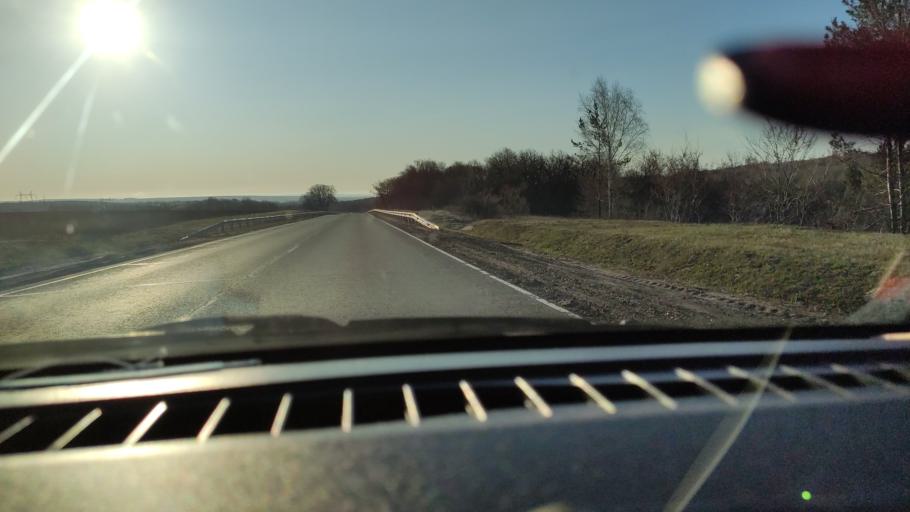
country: RU
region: Saratov
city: Vol'sk
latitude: 52.1037
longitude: 47.4471
